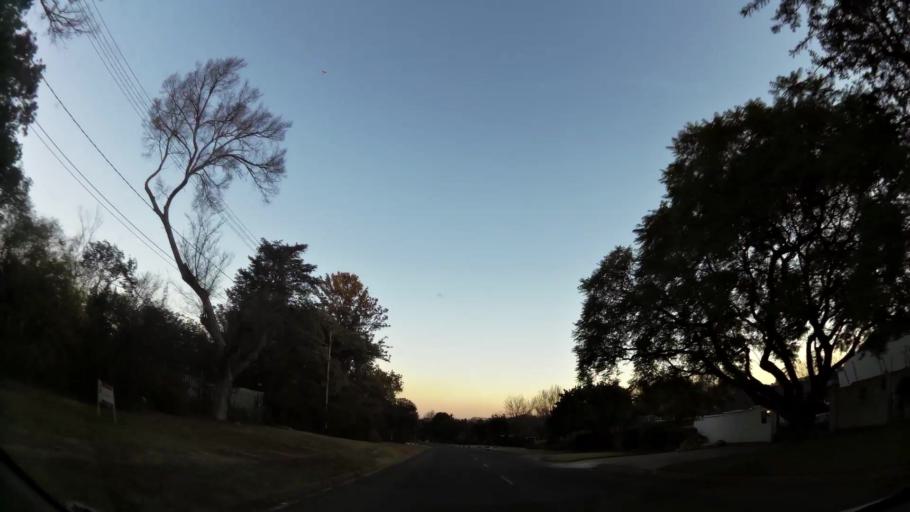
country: ZA
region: Gauteng
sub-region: City of Johannesburg Metropolitan Municipality
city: Roodepoort
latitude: -26.1575
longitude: 27.9077
